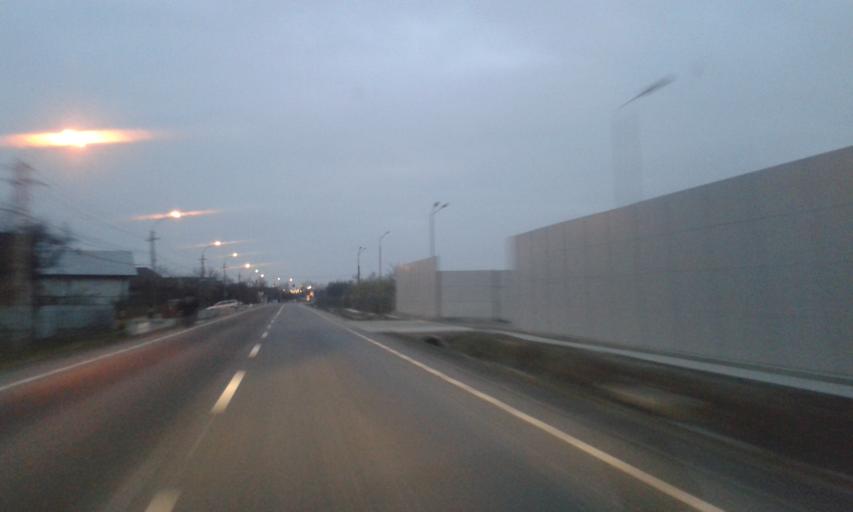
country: RO
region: Gorj
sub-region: Comuna Turcinesti
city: Turcinesti
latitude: 45.0924
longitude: 23.3264
